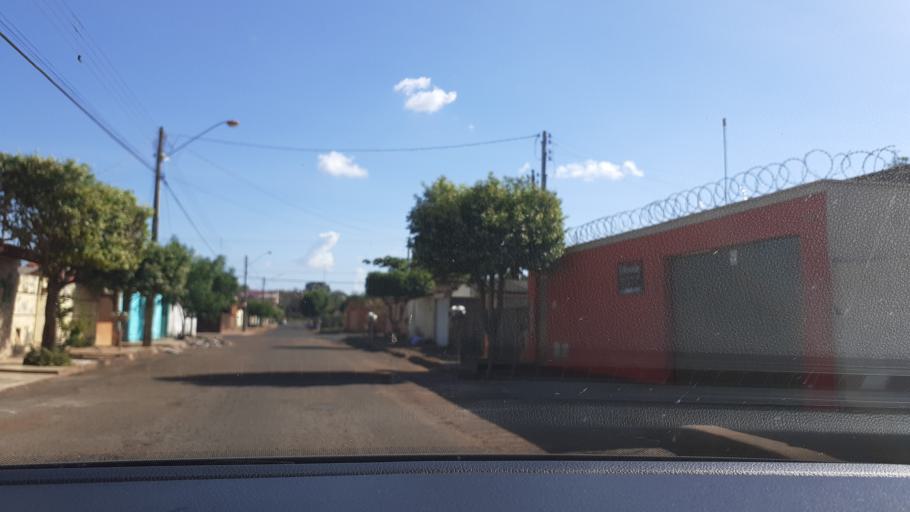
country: BR
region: Goias
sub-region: Itumbiara
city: Itumbiara
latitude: -18.4127
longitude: -49.2553
